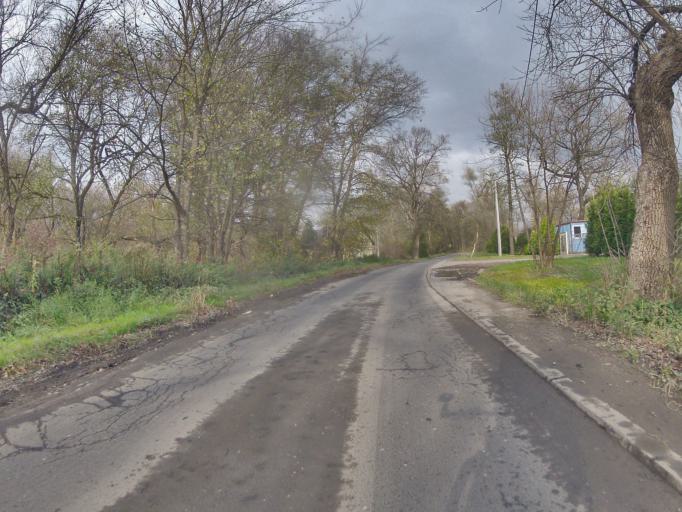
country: PL
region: Lesser Poland Voivodeship
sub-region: Powiat wielicki
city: Wegrzce Wielkie
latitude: 50.0575
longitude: 20.1017
